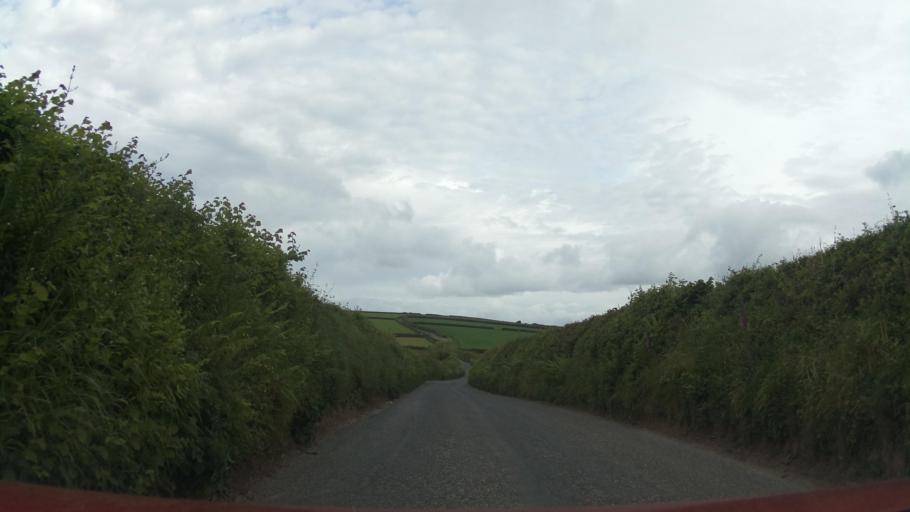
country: GB
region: England
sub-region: Devon
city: Dartmouth
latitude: 50.3211
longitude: -3.6369
